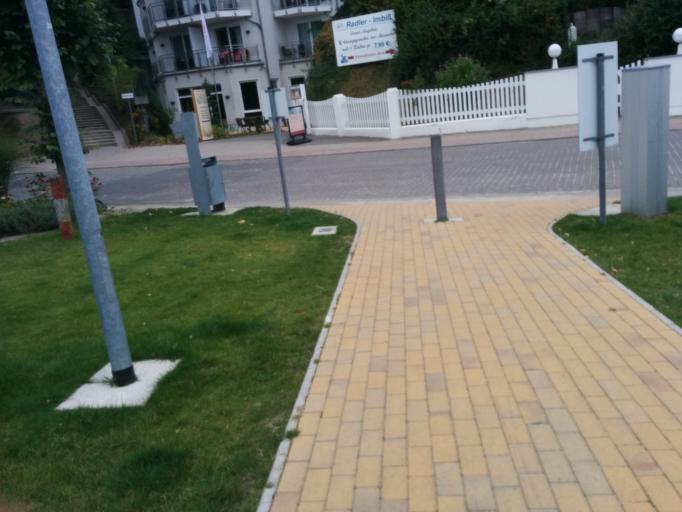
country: DE
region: Mecklenburg-Vorpommern
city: Loddin
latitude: 54.0411
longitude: 14.0296
